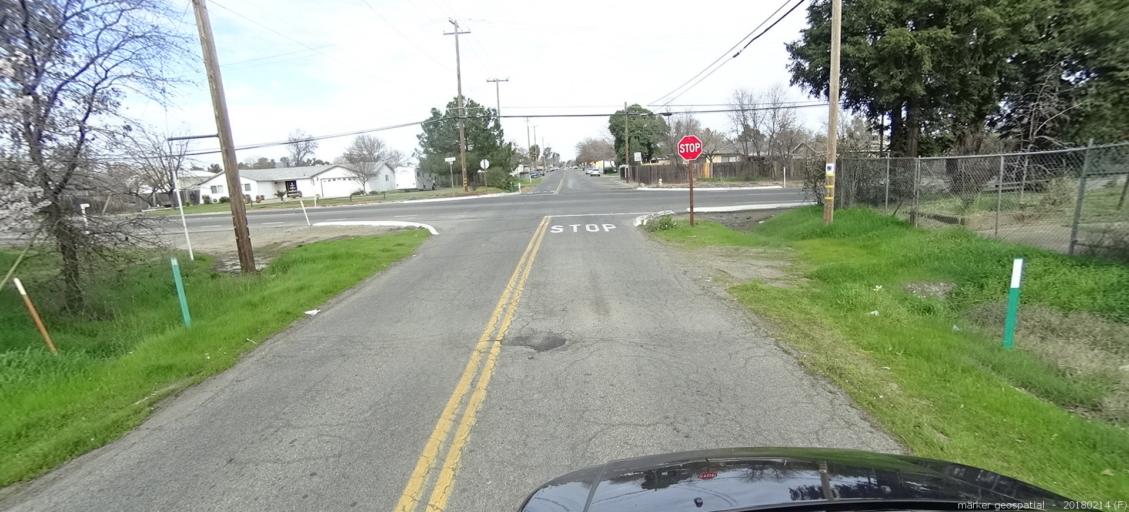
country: US
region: California
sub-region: Sacramento County
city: Rio Linda
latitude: 38.6837
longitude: -121.4662
